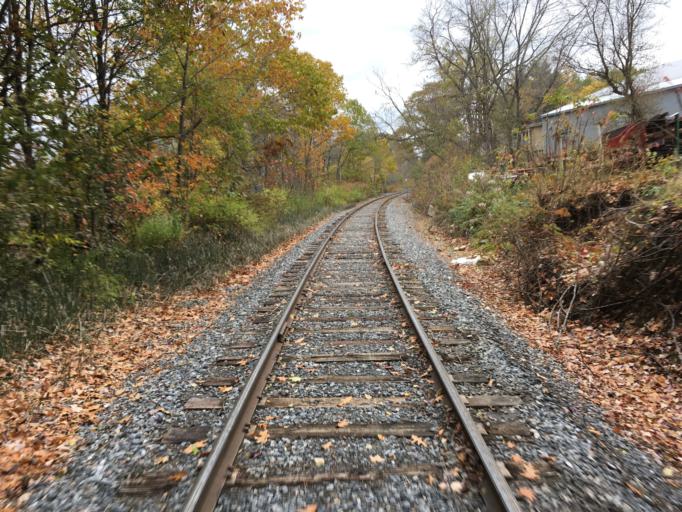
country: US
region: New Hampshire
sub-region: Grafton County
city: Woodsville
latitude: 44.1640
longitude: -72.0496
